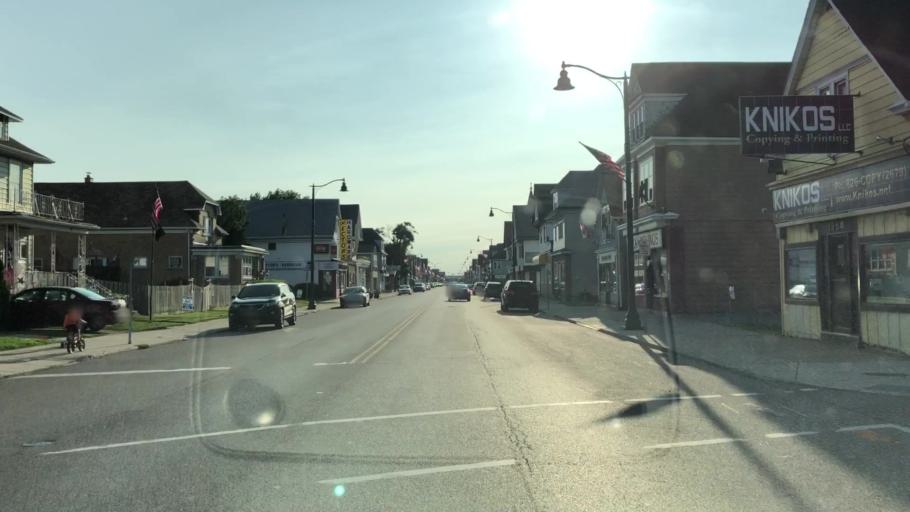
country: US
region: New York
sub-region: Erie County
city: West Seneca
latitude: 42.8718
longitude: -78.8031
